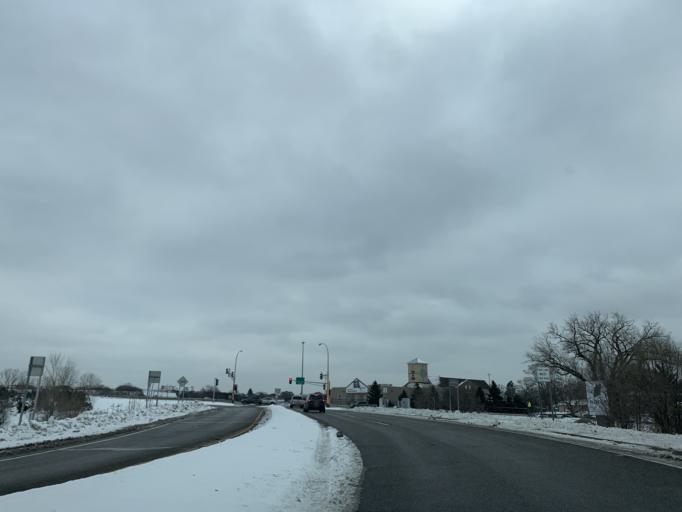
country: US
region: Minnesota
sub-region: Anoka County
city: Coon Rapids
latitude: 45.1517
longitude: -93.2764
